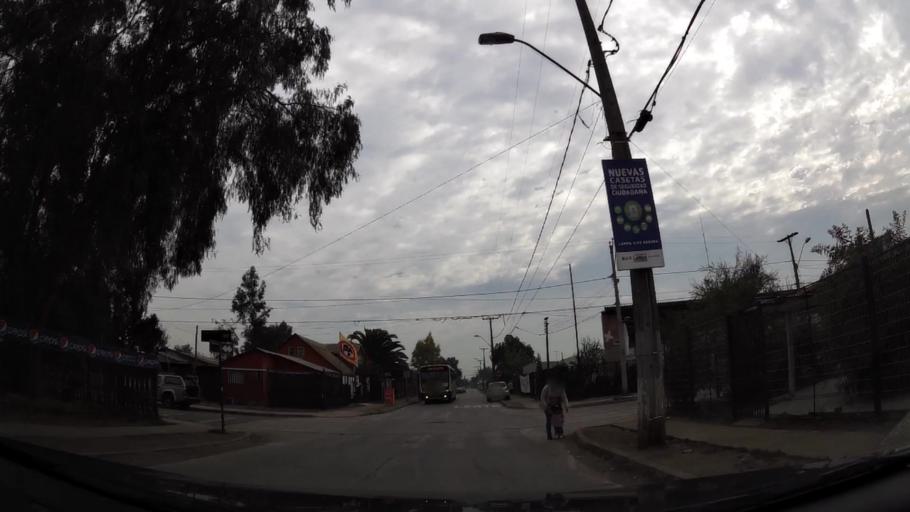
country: CL
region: Santiago Metropolitan
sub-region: Provincia de Chacabuco
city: Lampa
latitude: -33.2303
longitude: -70.8128
